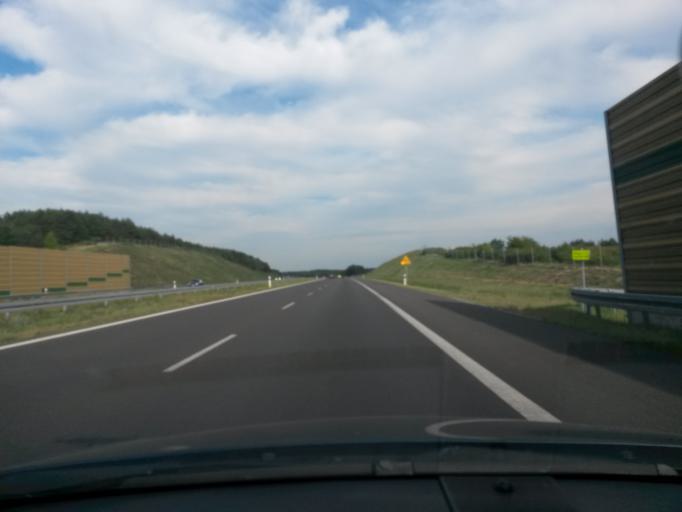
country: PL
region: Greater Poland Voivodeship
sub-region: Powiat turecki
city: Wladyslawow
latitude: 52.1439
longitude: 18.5181
